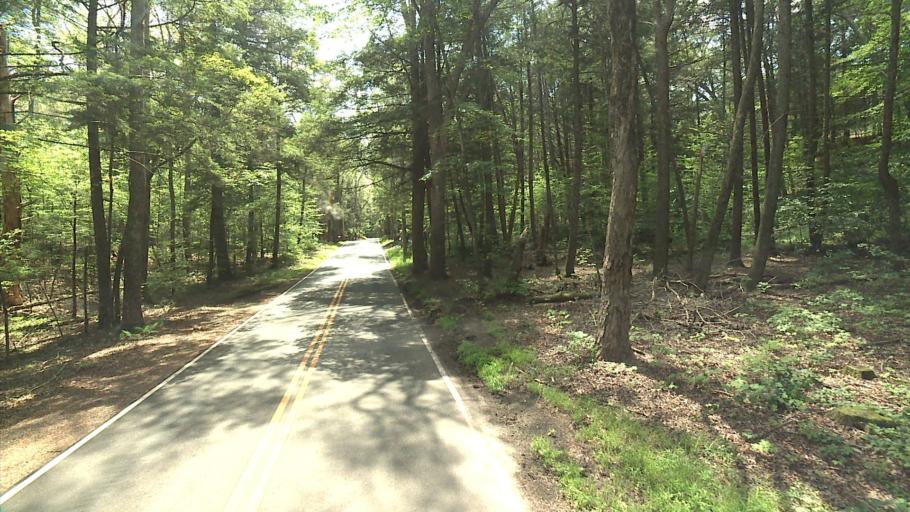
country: US
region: Connecticut
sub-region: Middlesex County
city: Essex Village
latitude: 41.4559
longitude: -72.3380
